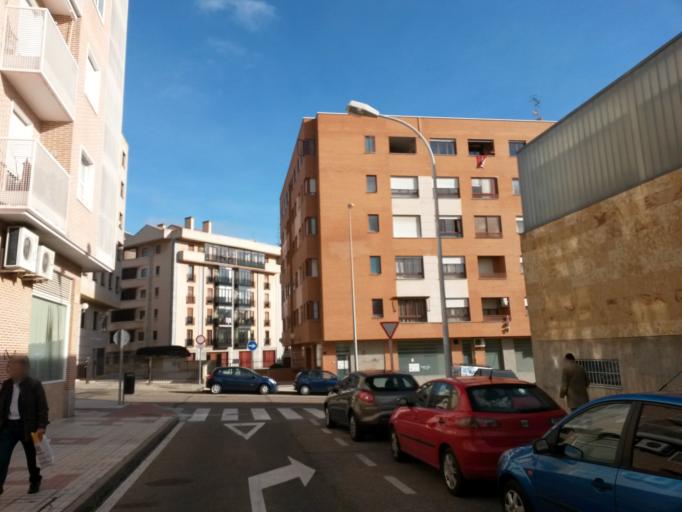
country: ES
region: Castille and Leon
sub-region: Provincia de Salamanca
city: Salamanca
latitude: 40.9787
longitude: -5.6547
